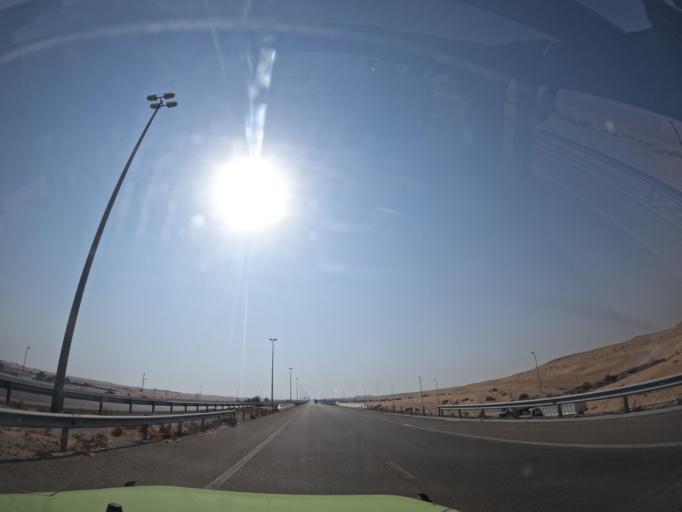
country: OM
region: Al Buraimi
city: Al Buraymi
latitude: 24.5117
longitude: 55.5658
